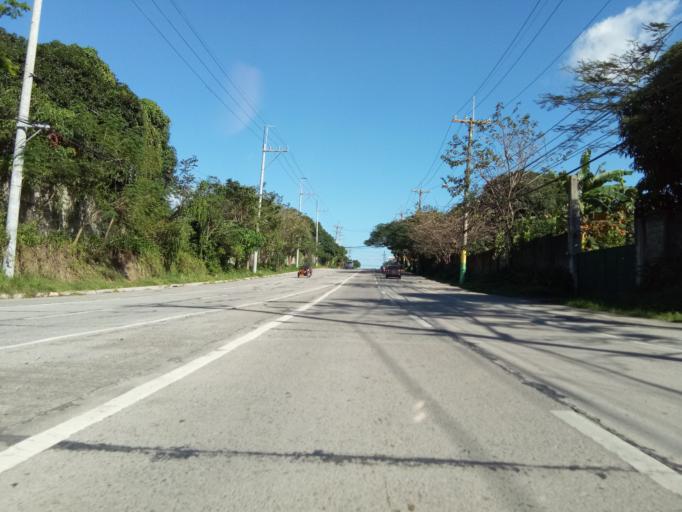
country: PH
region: Calabarzon
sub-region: Province of Cavite
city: Dasmarinas
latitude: 14.3516
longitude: 120.9541
